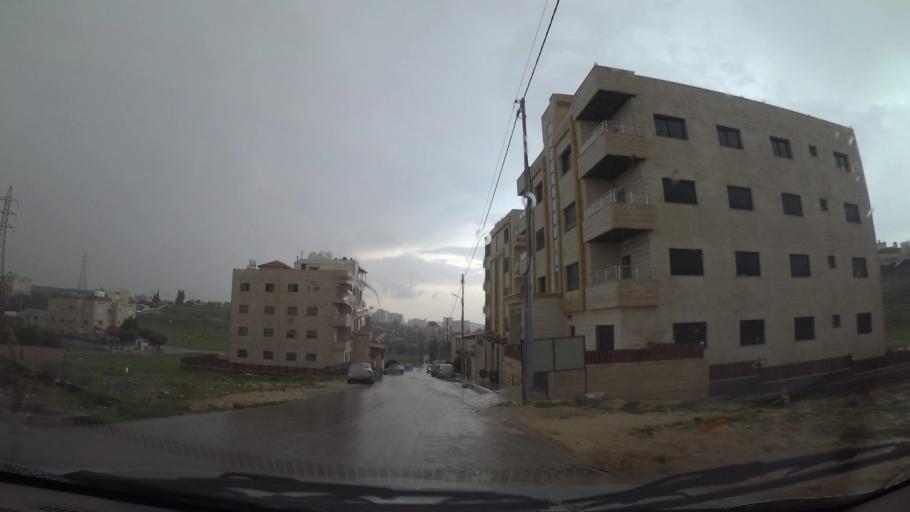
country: JO
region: Amman
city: Umm as Summaq
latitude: 31.8782
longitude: 35.8616
